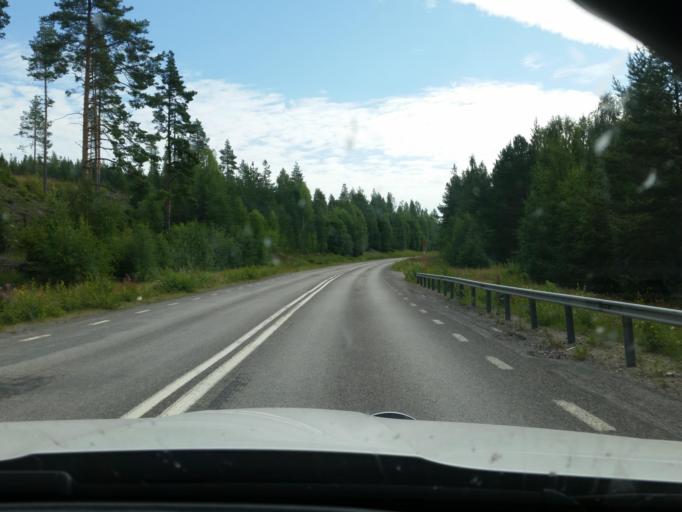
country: SE
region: Norrbotten
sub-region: Alvsbyns Kommun
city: AElvsbyn
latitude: 65.6814
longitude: 20.7882
